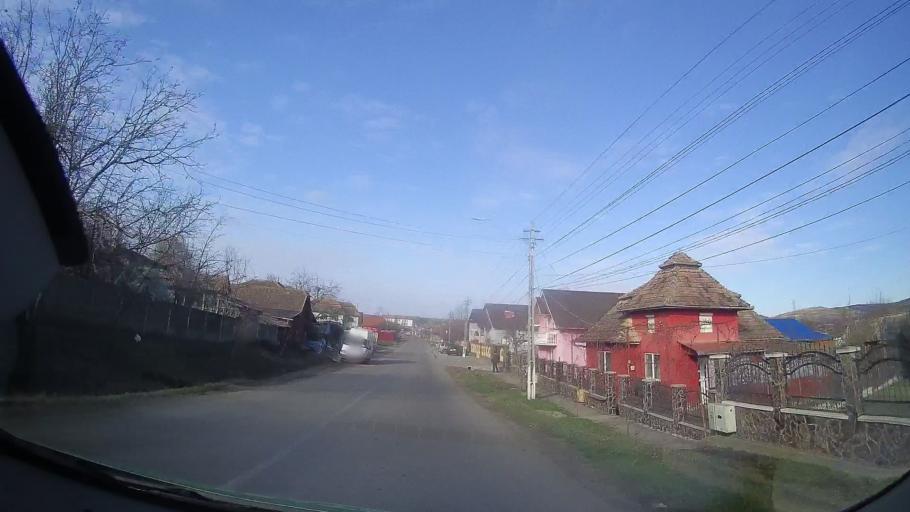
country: RO
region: Mures
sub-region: Comuna Valea Larga
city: Valea Larga
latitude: 46.6176
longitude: 24.0805
